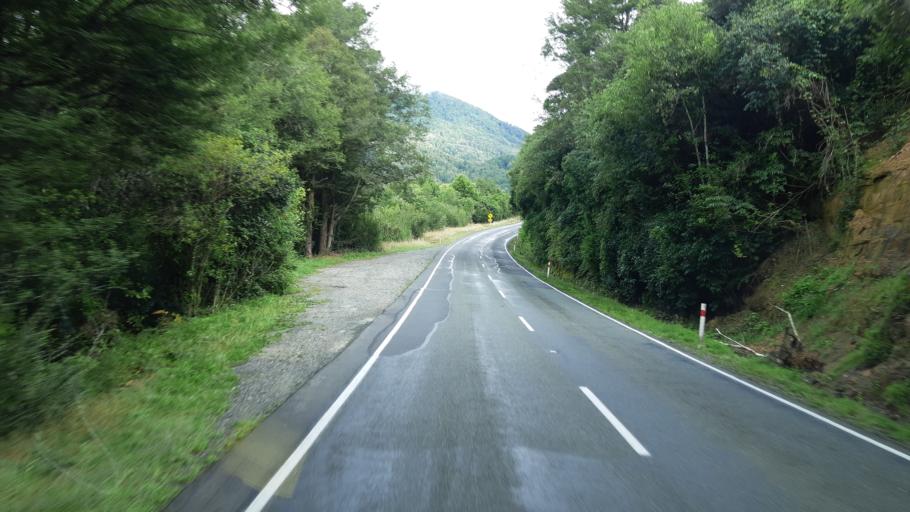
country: NZ
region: West Coast
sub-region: Buller District
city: Westport
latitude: -41.8112
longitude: 172.2283
